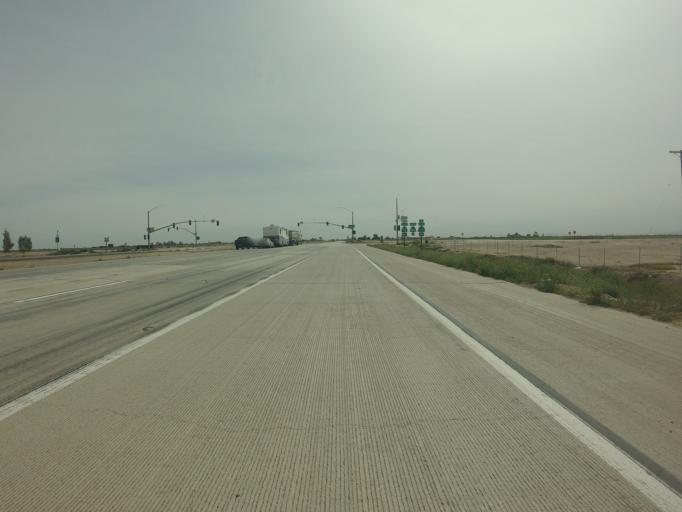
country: US
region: California
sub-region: Imperial County
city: Westmorland
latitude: 33.0000
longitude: -115.5898
